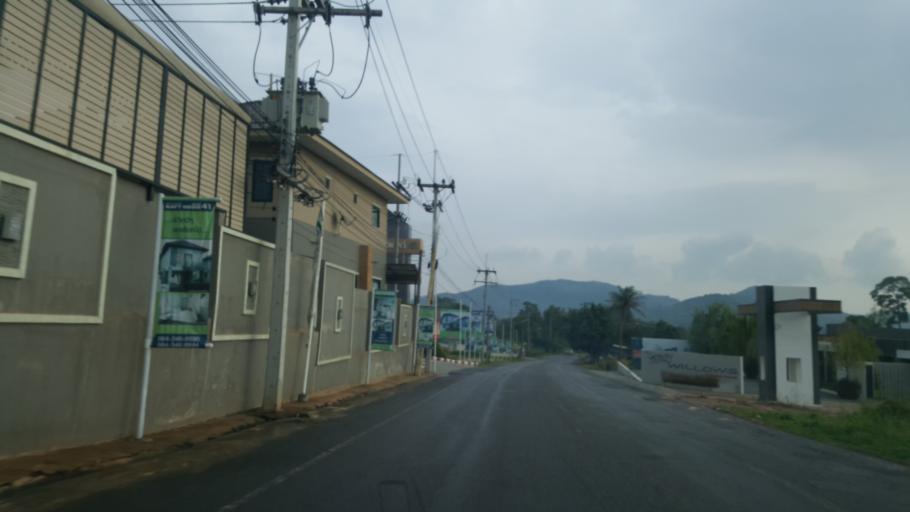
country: TH
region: Chon Buri
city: Sattahip
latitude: 12.7297
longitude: 100.9132
